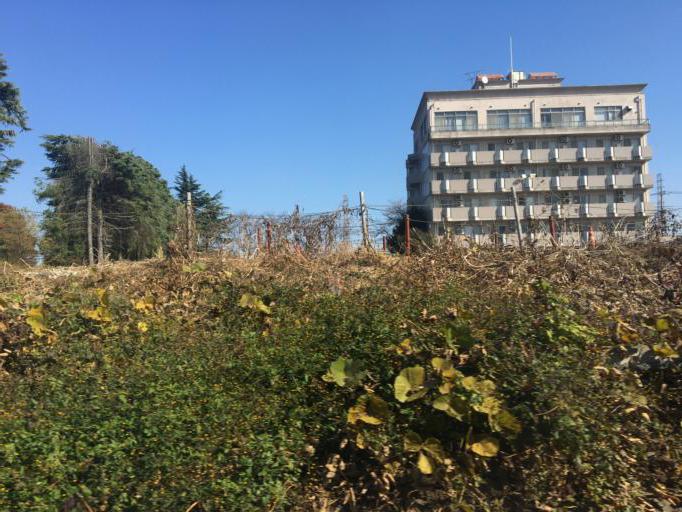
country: JP
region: Tochigi
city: Oyama
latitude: 36.3304
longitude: 139.8081
